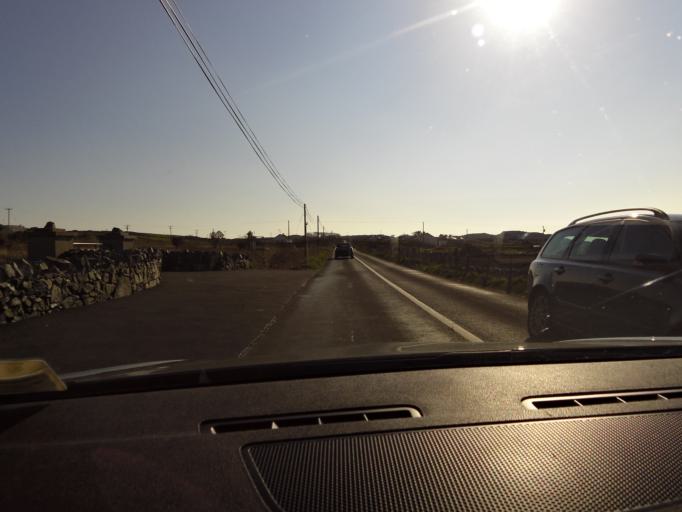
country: IE
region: Connaught
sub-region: County Galway
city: Clifden
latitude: 53.4399
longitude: -10.0664
